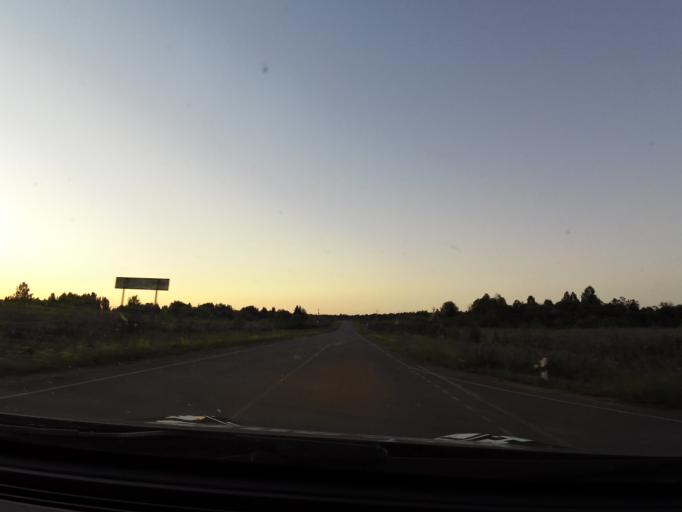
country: RU
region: Vologda
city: Vytegra
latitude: 60.9211
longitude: 36.0842
